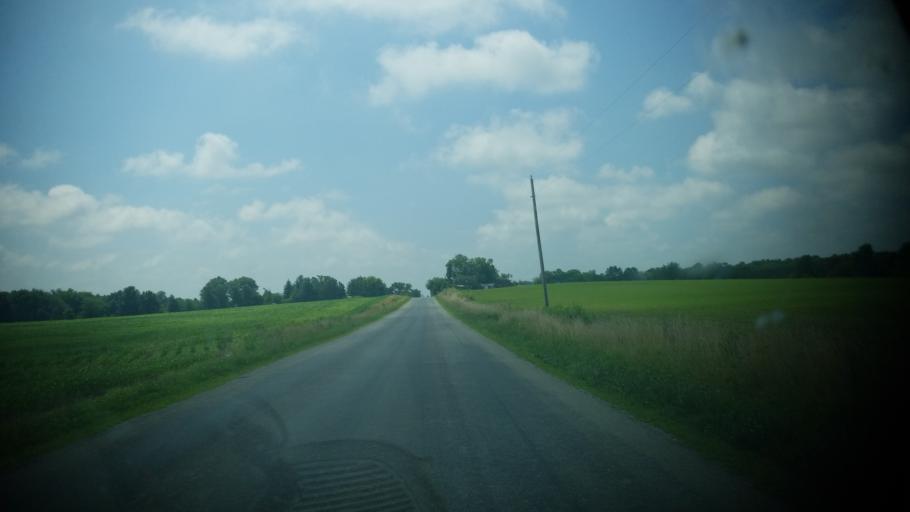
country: US
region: Illinois
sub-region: Wayne County
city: Fairfield
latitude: 38.5184
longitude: -88.3485
